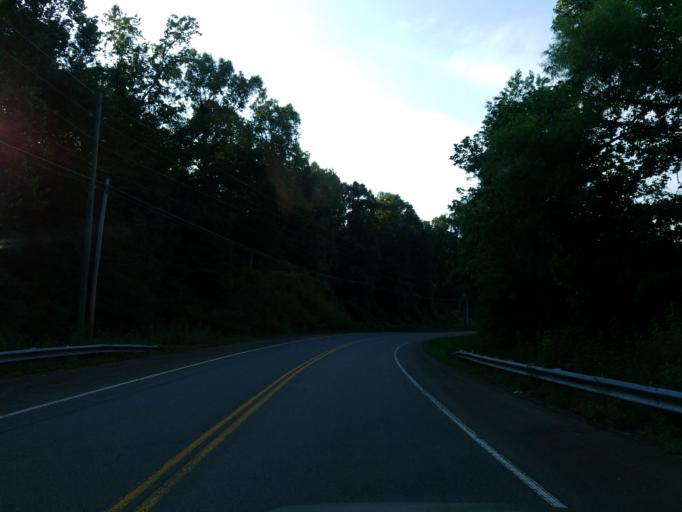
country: US
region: Georgia
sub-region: Pickens County
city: Jasper
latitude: 34.5423
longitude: -84.5416
